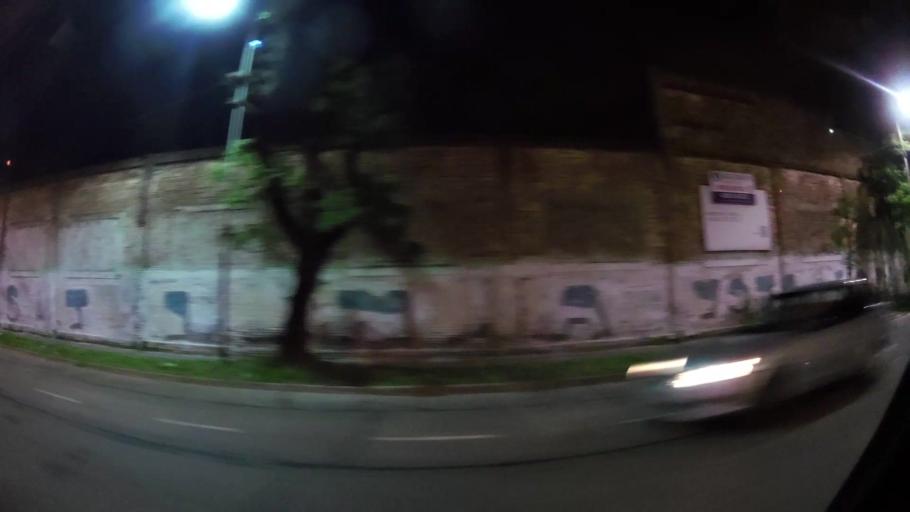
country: AR
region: Buenos Aires
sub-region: Partido de Avellaneda
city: Avellaneda
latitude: -34.7100
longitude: -58.3244
